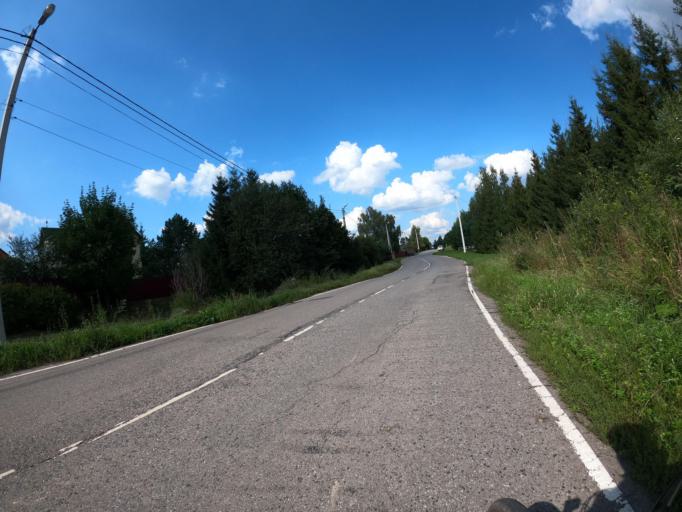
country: RU
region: Moskovskaya
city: Troitskoye
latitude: 55.2486
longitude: 38.5772
